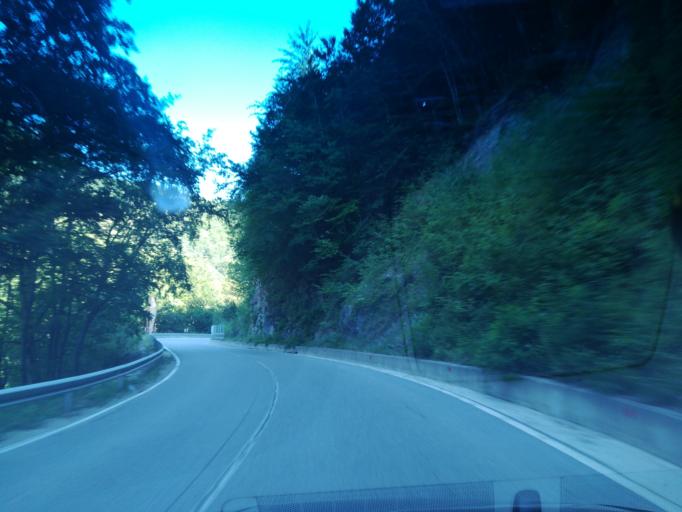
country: BG
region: Smolyan
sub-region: Obshtina Chepelare
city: Chepelare
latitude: 41.8105
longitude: 24.7058
